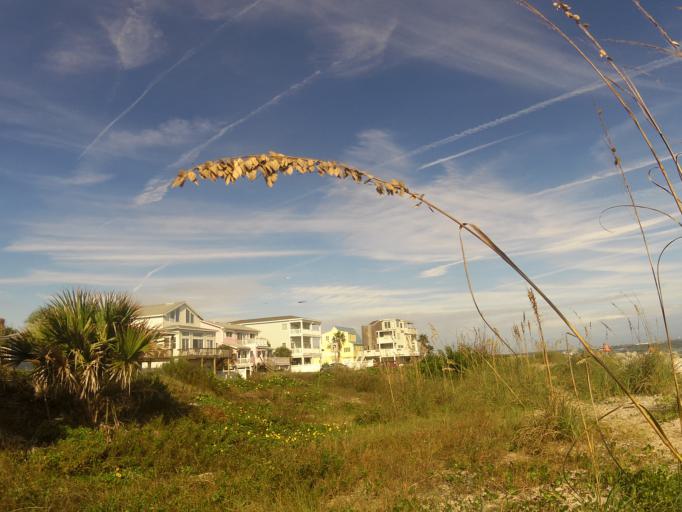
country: US
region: Florida
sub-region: Saint Johns County
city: Villano Beach
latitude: 29.9135
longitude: -81.2905
